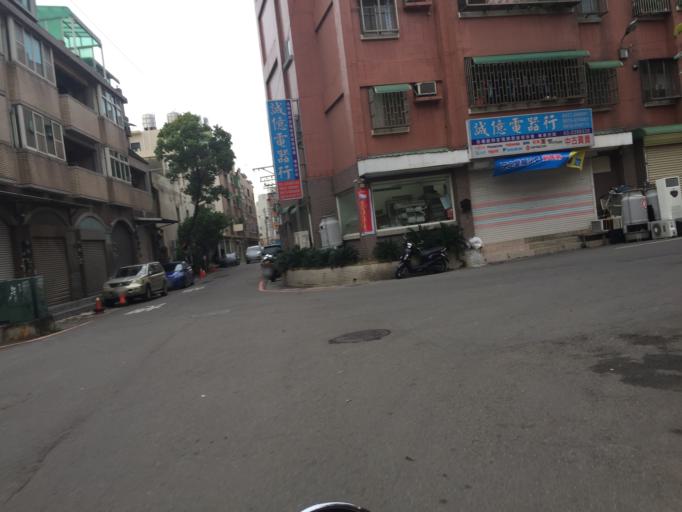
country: TW
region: Taiwan
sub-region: Hsinchu
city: Hsinchu
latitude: 24.7917
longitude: 120.9224
